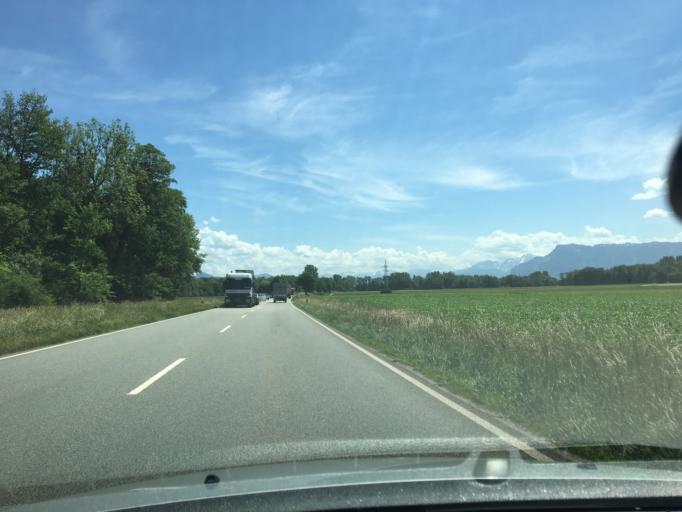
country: DE
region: Bavaria
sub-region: Upper Bavaria
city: Laufen
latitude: 47.8930
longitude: 12.9594
